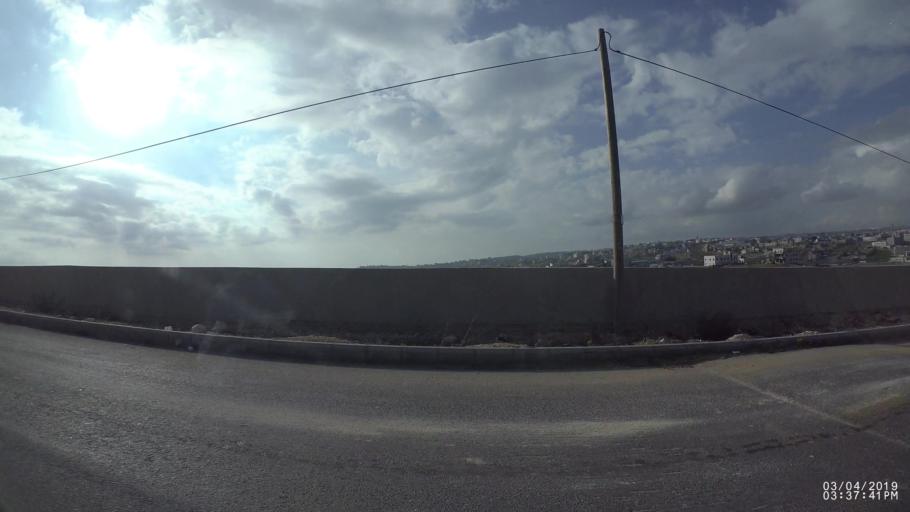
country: JO
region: Amman
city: Wadi as Sir
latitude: 31.9265
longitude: 35.8486
